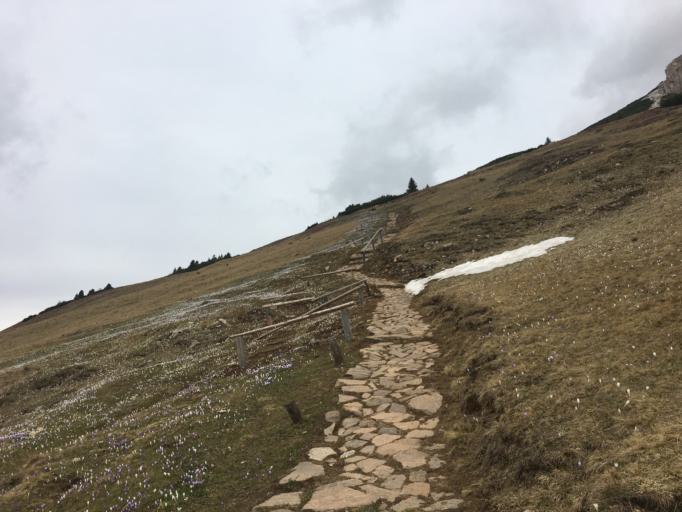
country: IT
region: Trentino-Alto Adige
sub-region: Provincia di Trento
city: Varena
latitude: 46.3483
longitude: 11.4483
